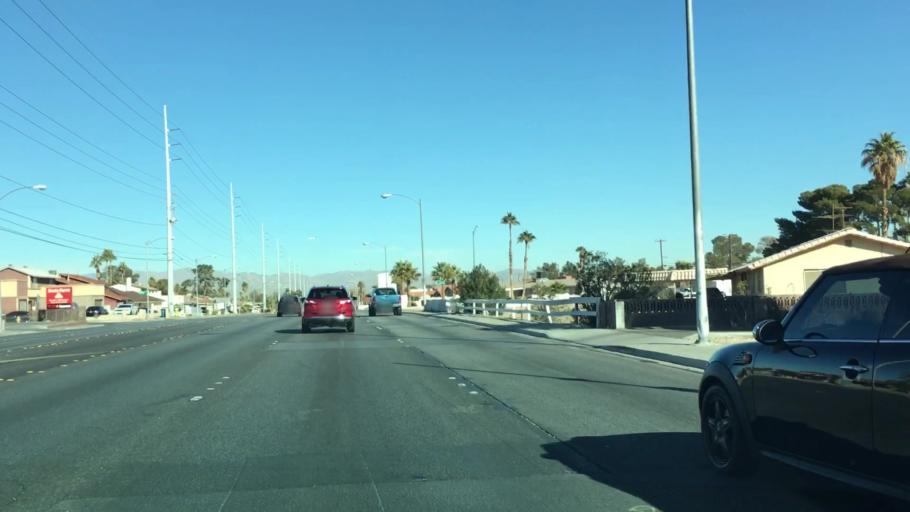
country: US
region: Nevada
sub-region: Clark County
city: Paradise
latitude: 36.0891
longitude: -115.1188
